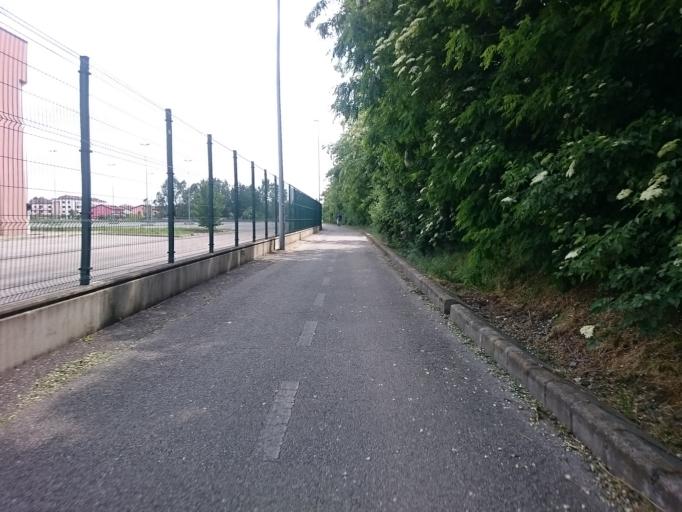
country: IT
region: Veneto
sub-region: Provincia di Rovigo
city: Rovigo
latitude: 45.0852
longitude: 11.7812
